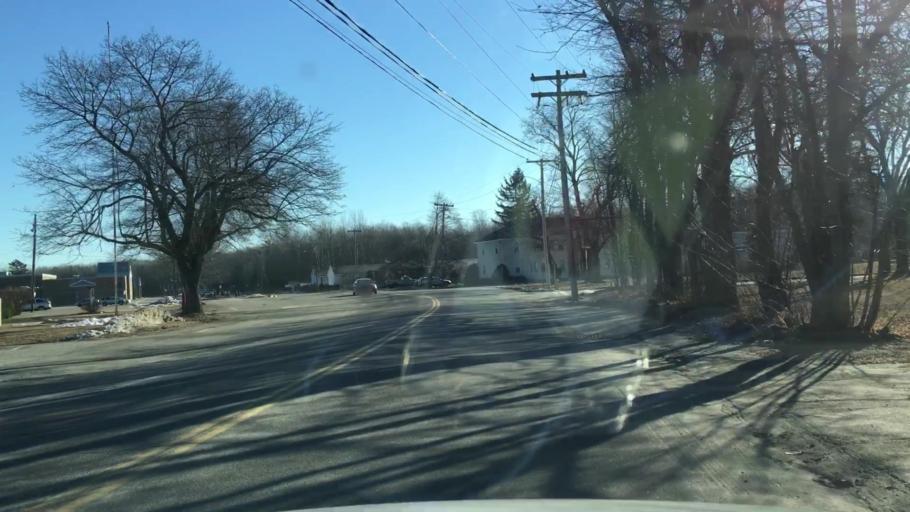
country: US
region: Maine
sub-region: Kennebec County
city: Winslow
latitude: 44.5508
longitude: -69.6218
